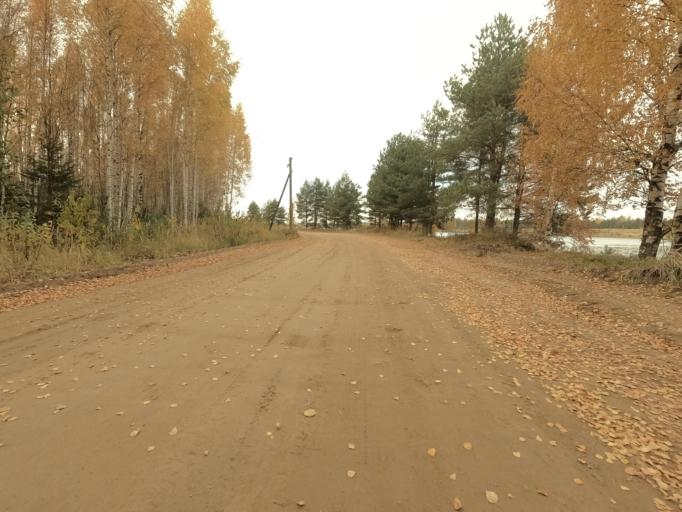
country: RU
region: Leningrad
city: Priladozhskiy
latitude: 59.7124
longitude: 31.3533
